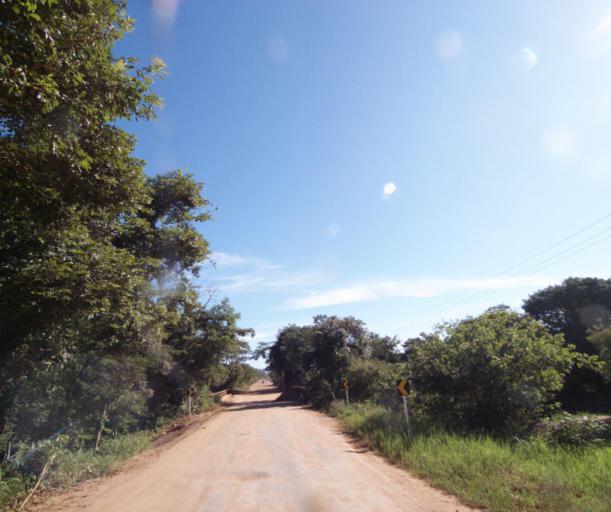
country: BR
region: Bahia
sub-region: Sao Felix Do Coribe
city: Santa Maria da Vitoria
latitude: -13.6455
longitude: -44.4419
